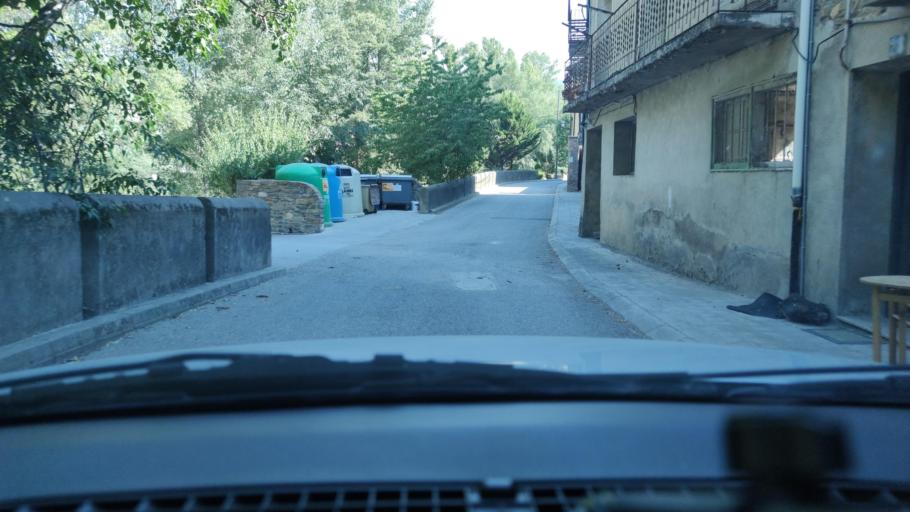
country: ES
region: Catalonia
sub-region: Provincia de Lleida
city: Senterada
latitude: 42.2444
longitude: 0.9713
